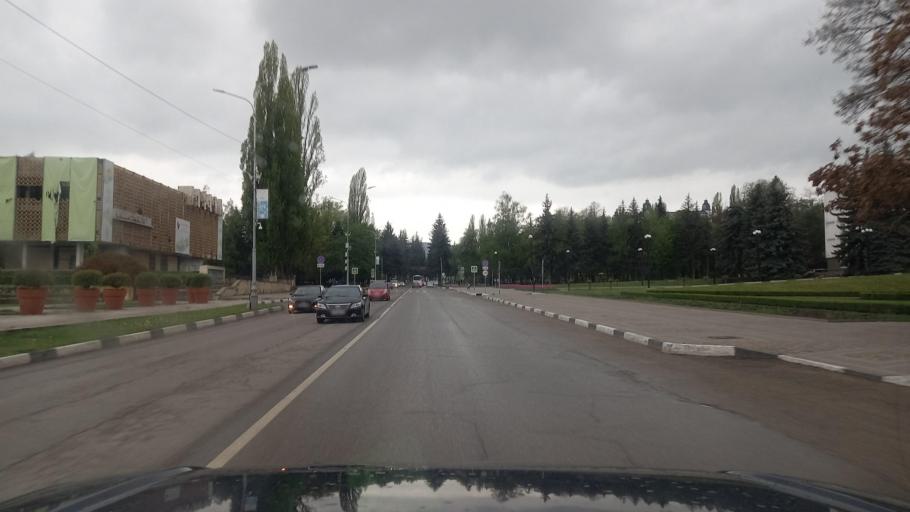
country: RU
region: Stavropol'skiy
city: Kislovodsk
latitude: 43.9132
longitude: 42.7188
